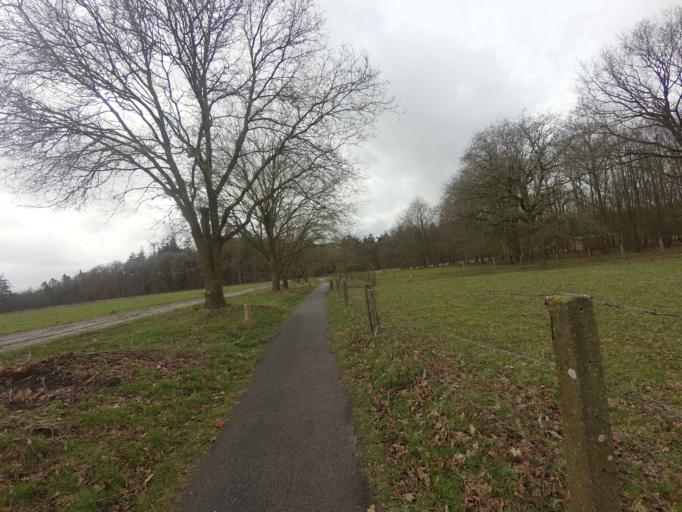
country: NL
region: Friesland
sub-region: Gemeente Gaasterlan-Sleat
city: Oudemirdum
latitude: 52.8657
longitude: 5.5316
